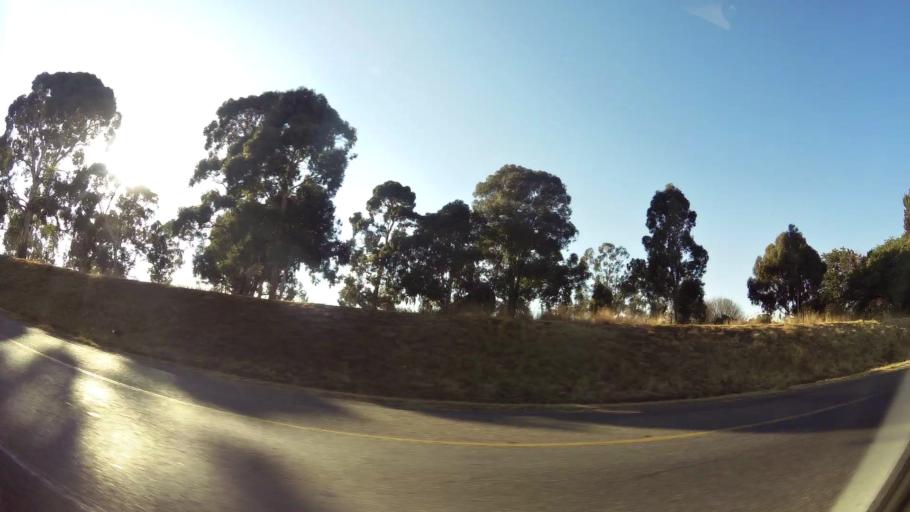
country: ZA
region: Gauteng
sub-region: Ekurhuleni Metropolitan Municipality
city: Germiston
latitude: -26.3256
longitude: 28.1127
